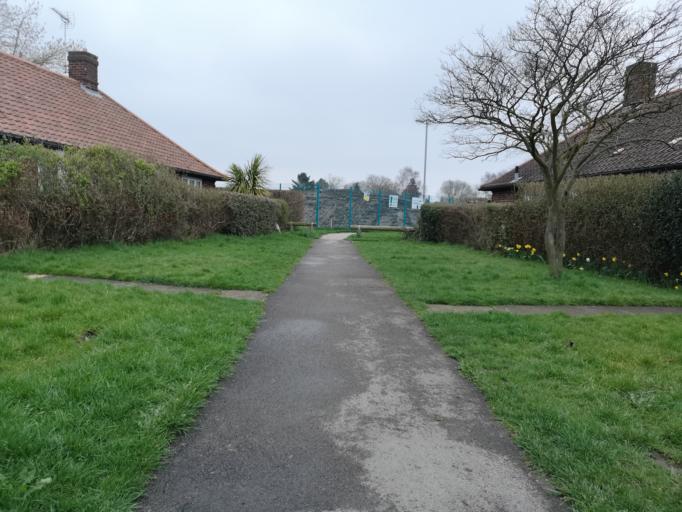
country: GB
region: England
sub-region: City of York
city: Haxby
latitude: 53.9888
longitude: -1.0761
